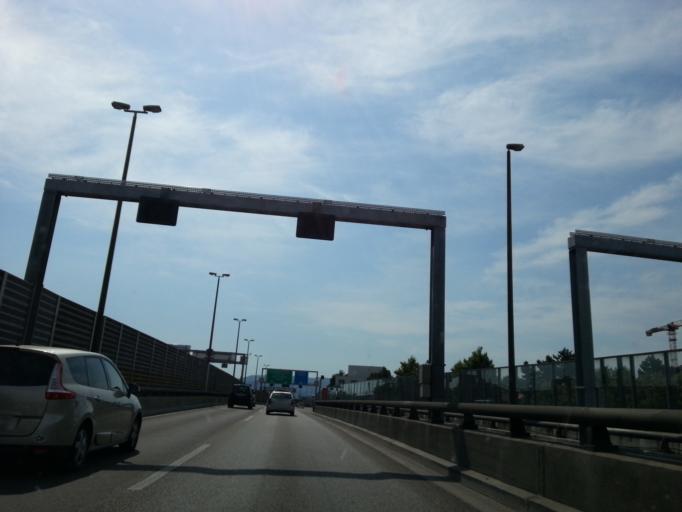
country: CH
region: Basel-Landschaft
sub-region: Bezirk Arlesheim
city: Birsfelden
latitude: 47.5630
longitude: 7.6101
